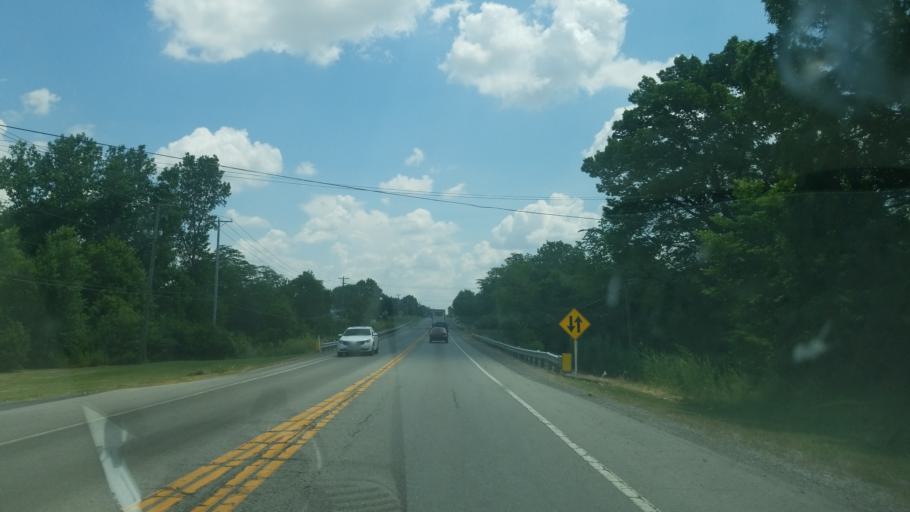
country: US
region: Ohio
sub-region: Allen County
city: Lima
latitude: 40.7310
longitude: -84.0425
